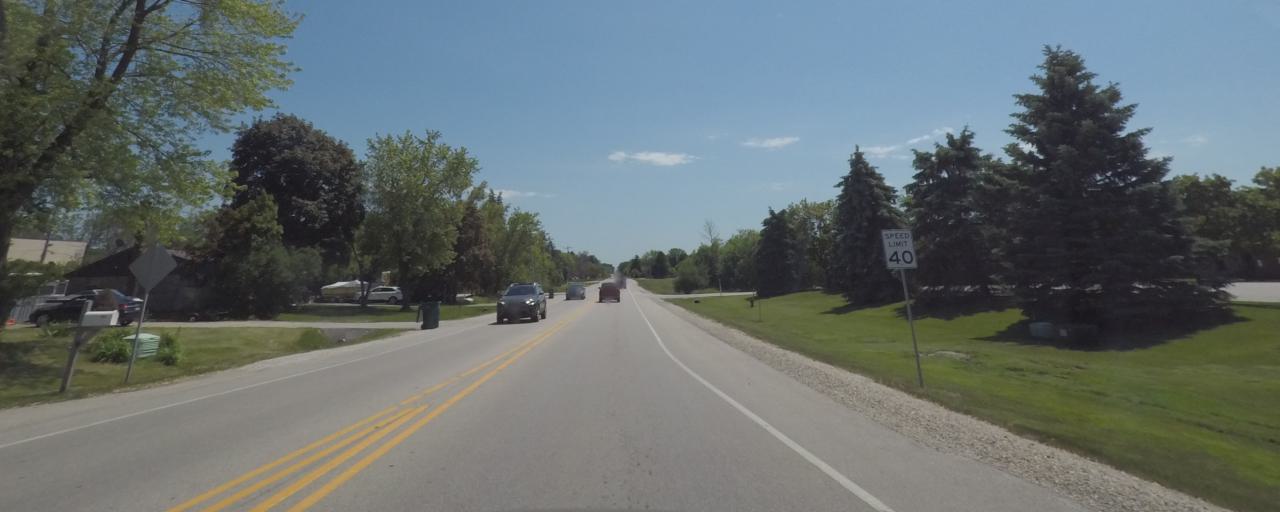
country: US
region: Wisconsin
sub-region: Waukesha County
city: New Berlin
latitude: 42.9926
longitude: -88.1280
